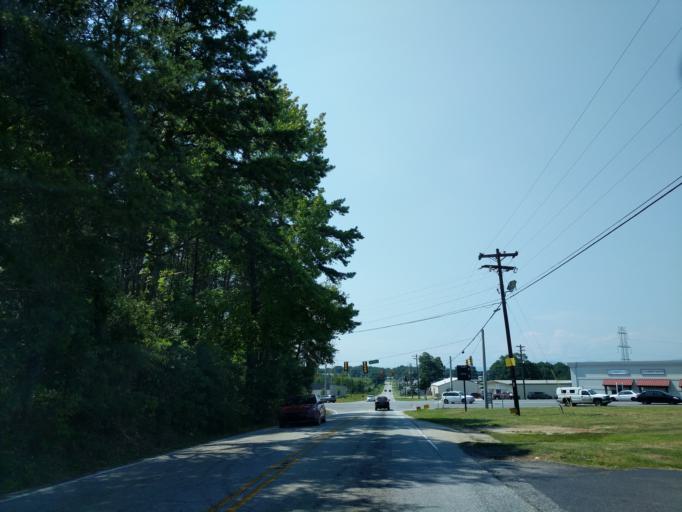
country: US
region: South Carolina
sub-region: Spartanburg County
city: Duncan
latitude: 34.9542
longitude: -82.1687
